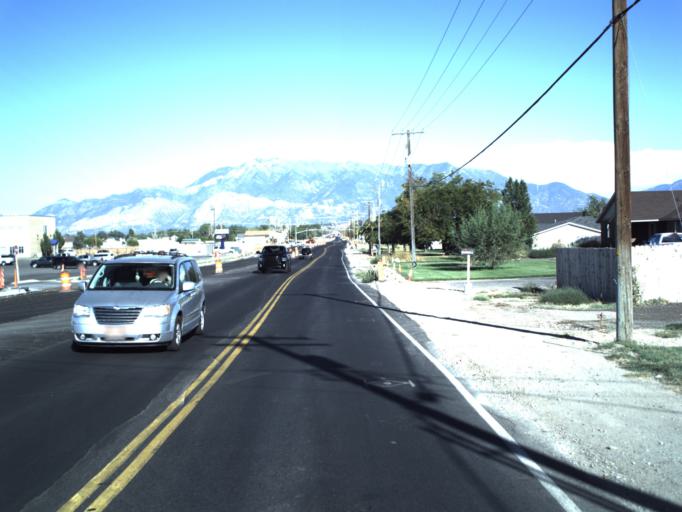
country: US
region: Utah
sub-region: Weber County
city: Hooper
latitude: 41.1907
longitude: -112.0982
